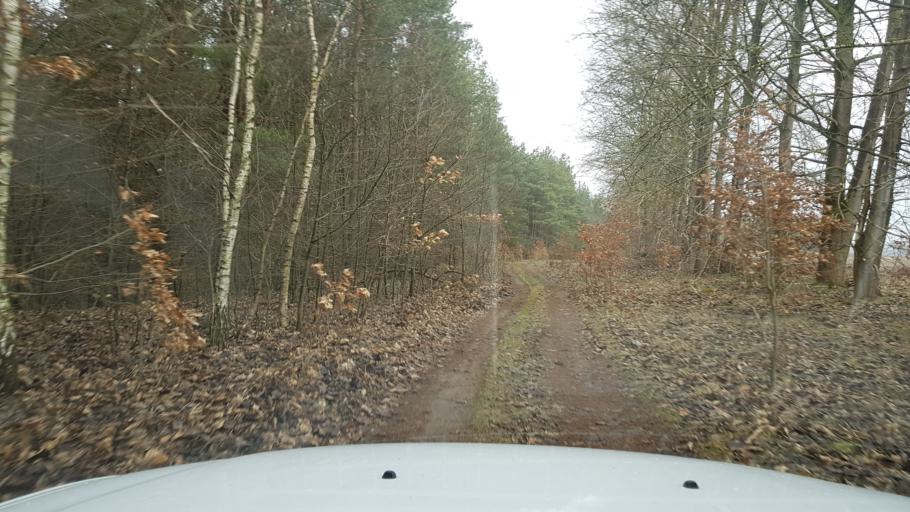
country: PL
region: West Pomeranian Voivodeship
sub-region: Powiat drawski
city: Czaplinek
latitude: 53.5710
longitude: 16.2493
